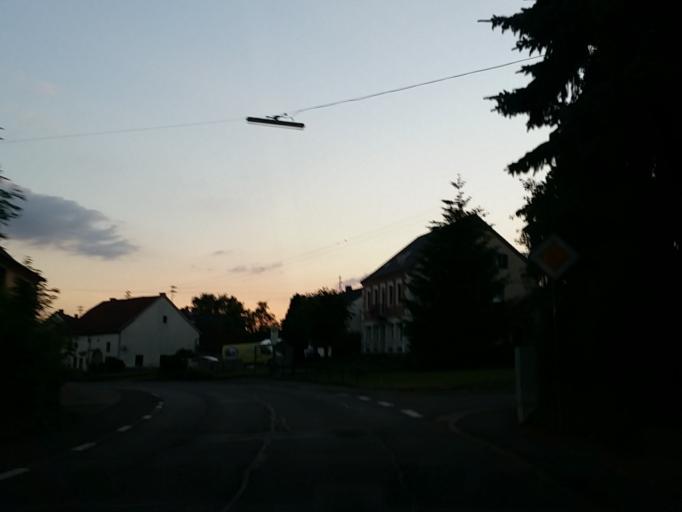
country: DE
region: Saarland
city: Wadern
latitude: 49.5257
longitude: 6.9172
